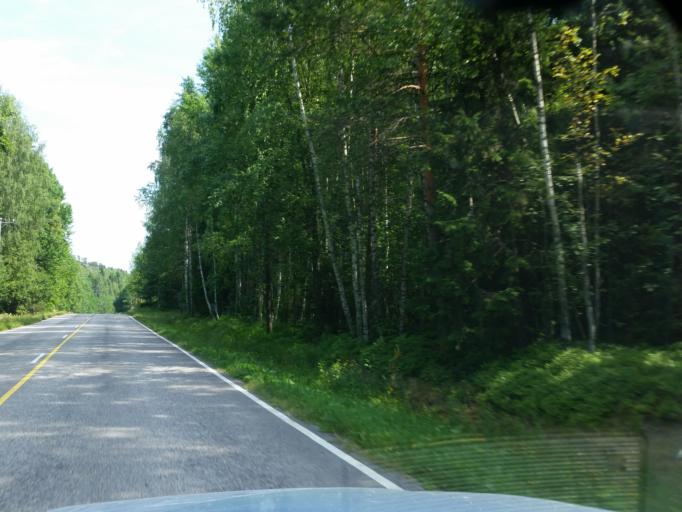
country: FI
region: Varsinais-Suomi
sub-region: Aboland-Turunmaa
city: Nagu
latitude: 60.2161
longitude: 22.0844
